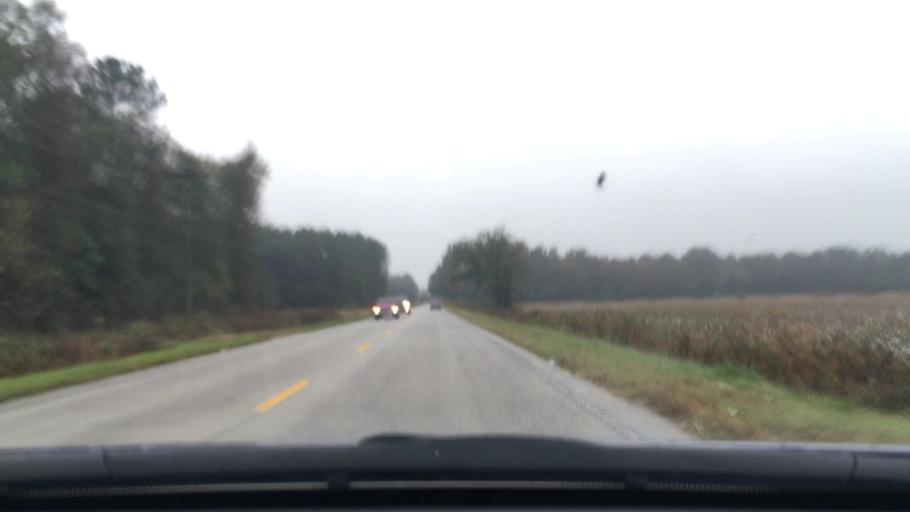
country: US
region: South Carolina
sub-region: Florence County
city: Timmonsville
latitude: 34.2292
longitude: -79.9887
